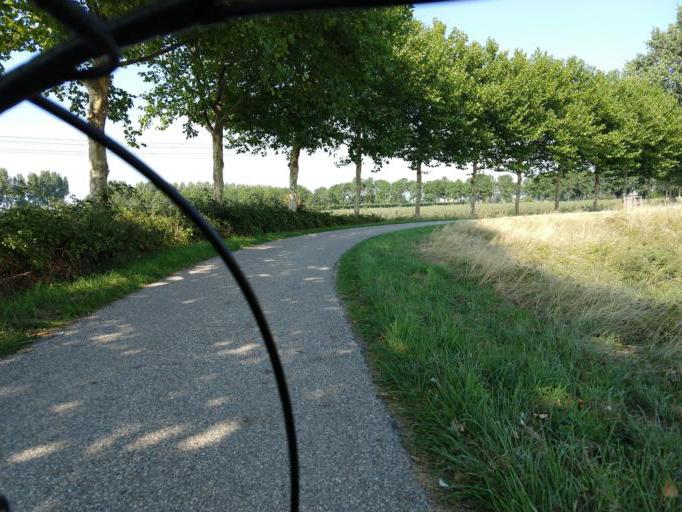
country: NL
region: Zeeland
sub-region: Gemeente Terneuzen
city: Terneuzen
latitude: 51.4155
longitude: 3.8435
